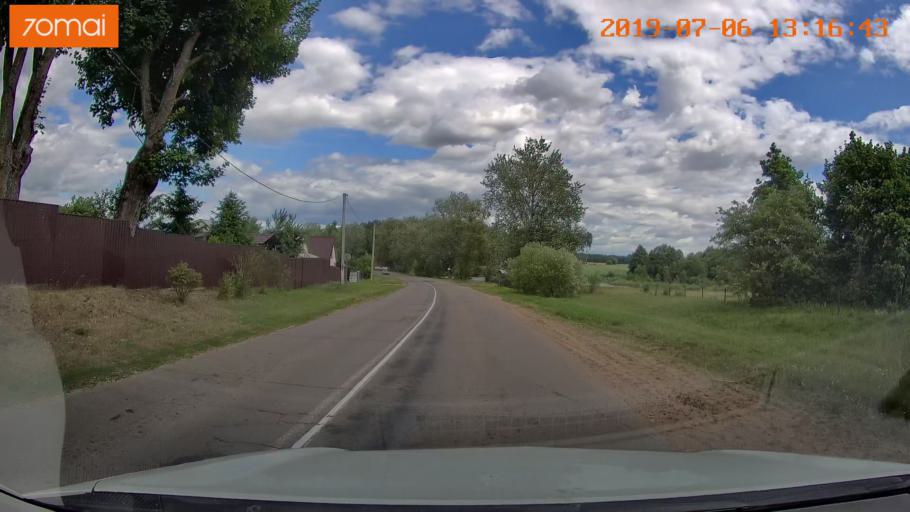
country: BY
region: Minsk
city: Enyerhyetykaw
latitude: 53.6609
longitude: 27.0106
